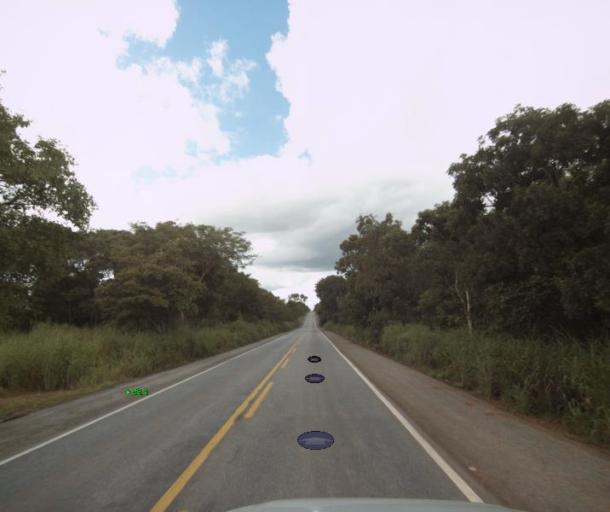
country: BR
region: Goias
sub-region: Porangatu
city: Porangatu
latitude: -13.2746
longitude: -49.1303
